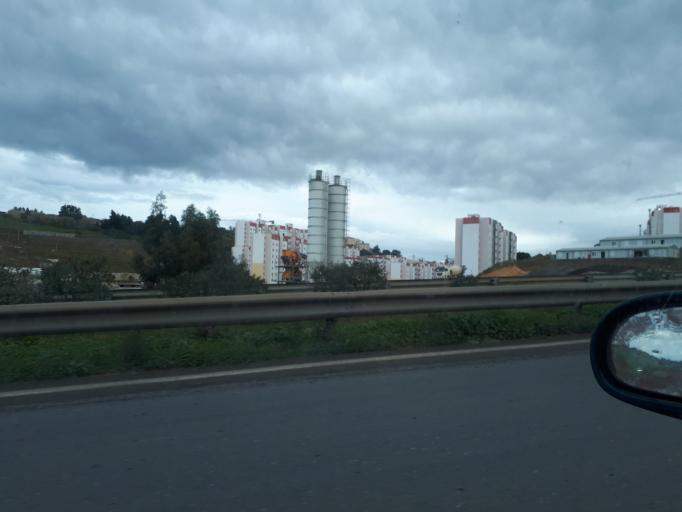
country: DZ
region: Tipaza
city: Douera
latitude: 36.7072
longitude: 2.9320
